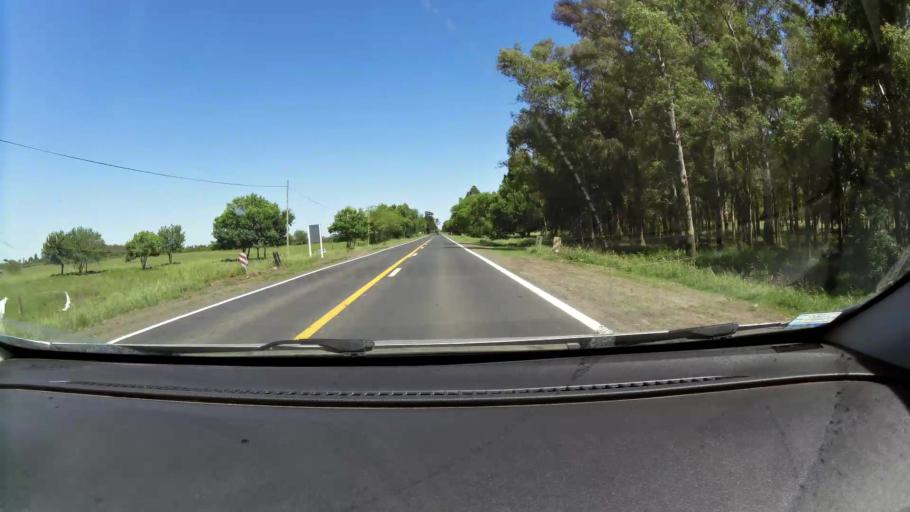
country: AR
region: Santa Fe
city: Esperanza
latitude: -31.4365
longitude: -60.9551
